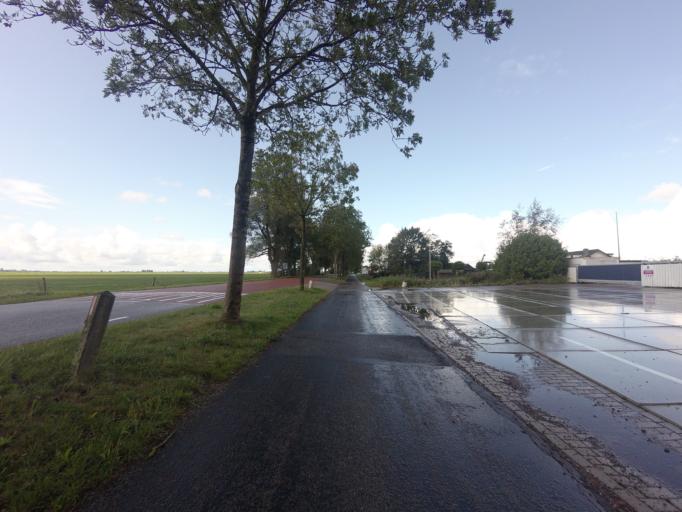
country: NL
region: Friesland
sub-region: Gemeente Boarnsterhim
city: Warten
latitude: 53.1495
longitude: 5.8876
